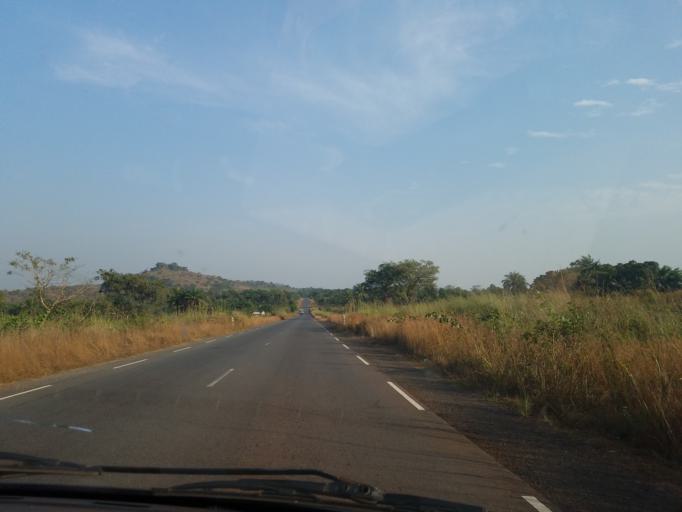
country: GN
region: Boke
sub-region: Boffa
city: Boffa
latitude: 10.3491
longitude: -14.2485
